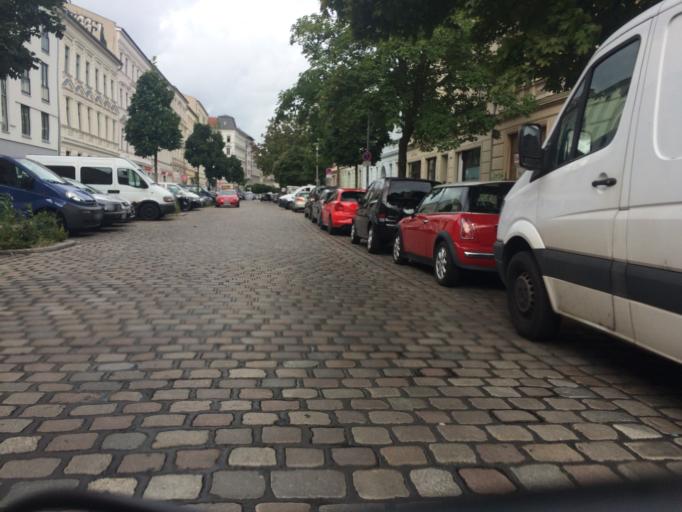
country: DE
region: Berlin
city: Rummelsburg
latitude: 52.5036
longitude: 13.4759
